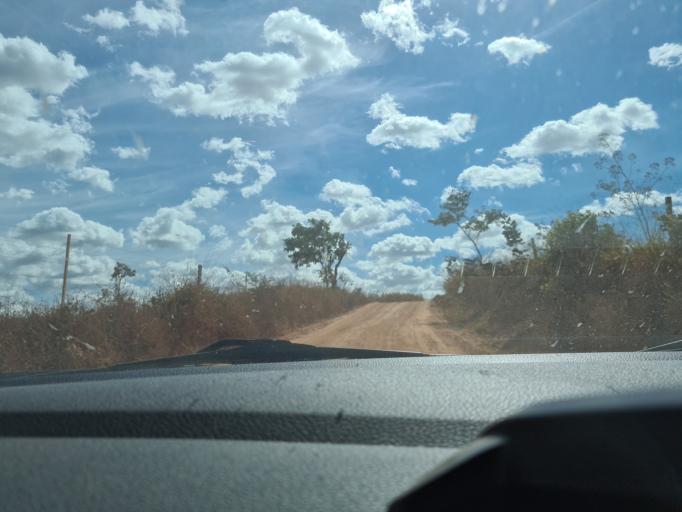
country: BR
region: Goias
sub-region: Silvania
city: Silvania
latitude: -16.5338
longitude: -48.5868
